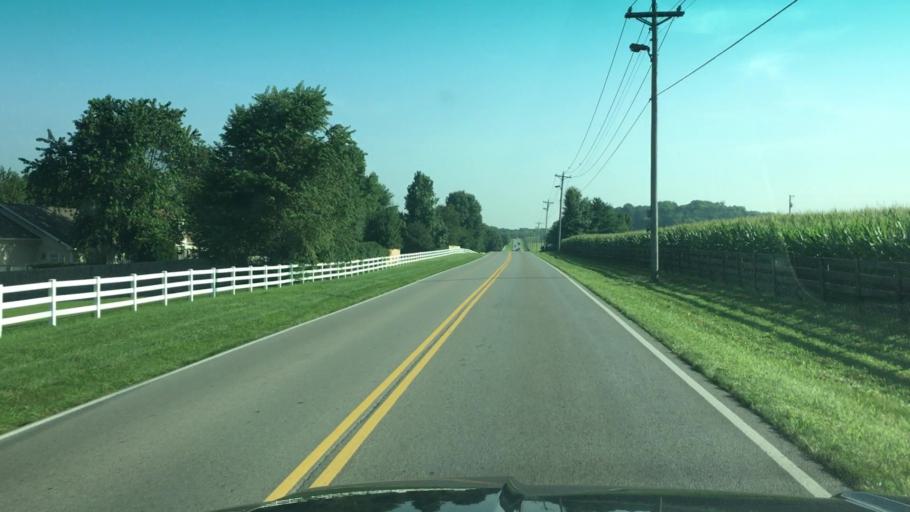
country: US
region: Tennessee
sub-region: Williamson County
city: Thompson's Station
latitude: 35.7807
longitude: -86.8791
